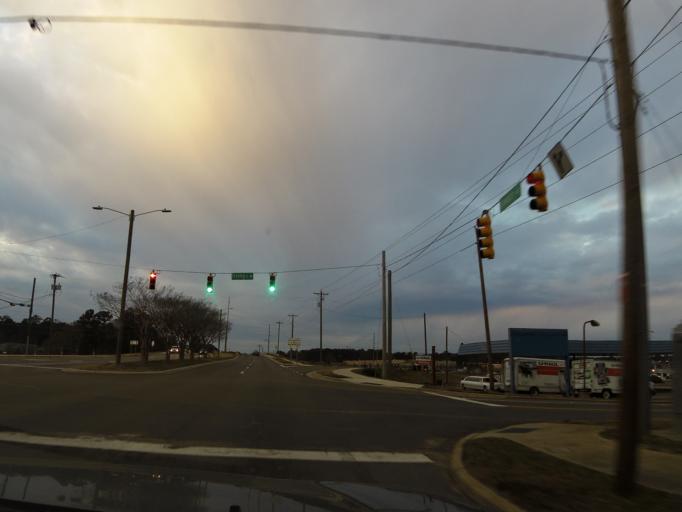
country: US
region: North Carolina
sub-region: Nash County
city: Rocky Mount
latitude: 35.9560
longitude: -77.8224
